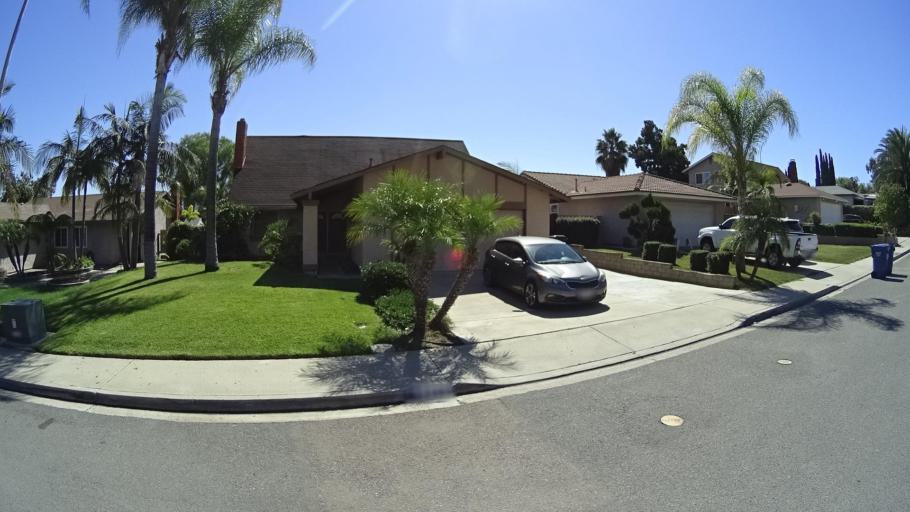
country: US
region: California
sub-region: San Diego County
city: La Presa
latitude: 32.6932
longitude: -117.0183
